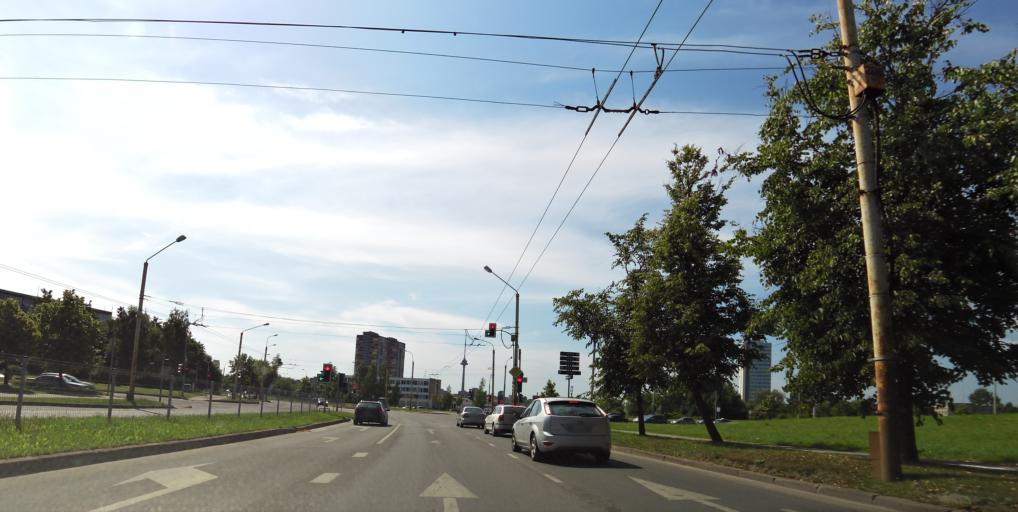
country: LT
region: Vilnius County
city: Justiniskes
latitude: 54.7066
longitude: 25.2154
